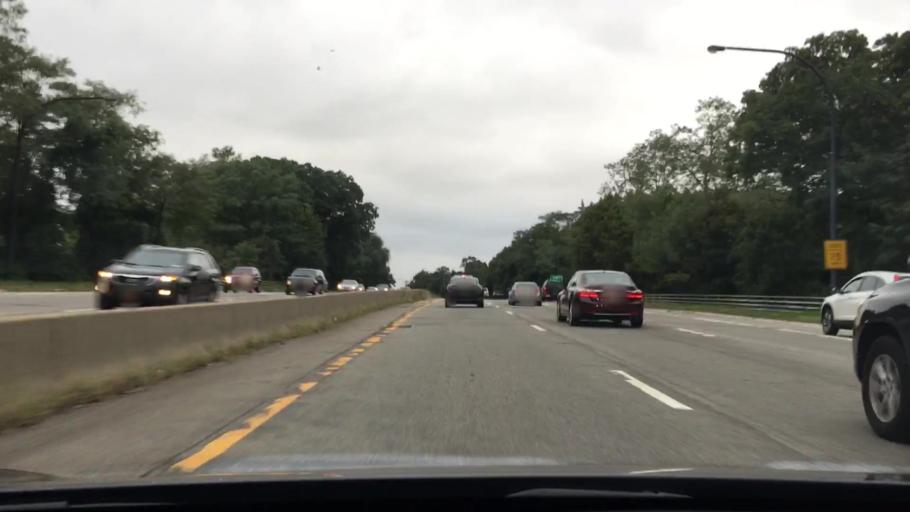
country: US
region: New York
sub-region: Nassau County
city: Roslyn Heights
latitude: 40.7818
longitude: -73.6487
